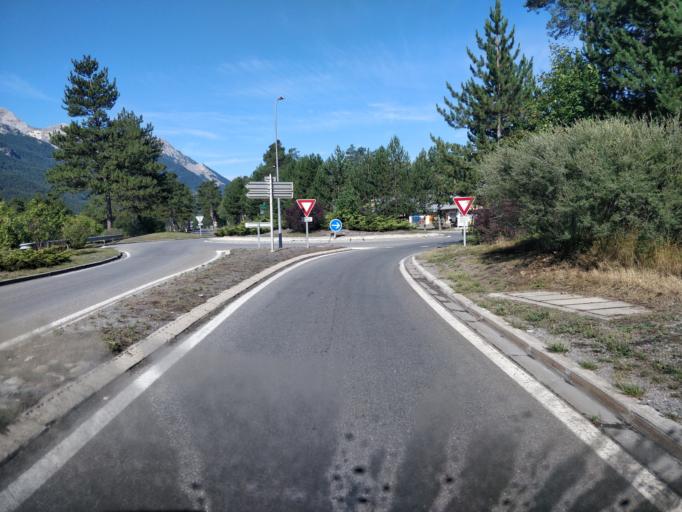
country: FR
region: Provence-Alpes-Cote d'Azur
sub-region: Departement des Alpes-de-Haute-Provence
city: Barcelonnette
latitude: 44.3864
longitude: 6.6299
